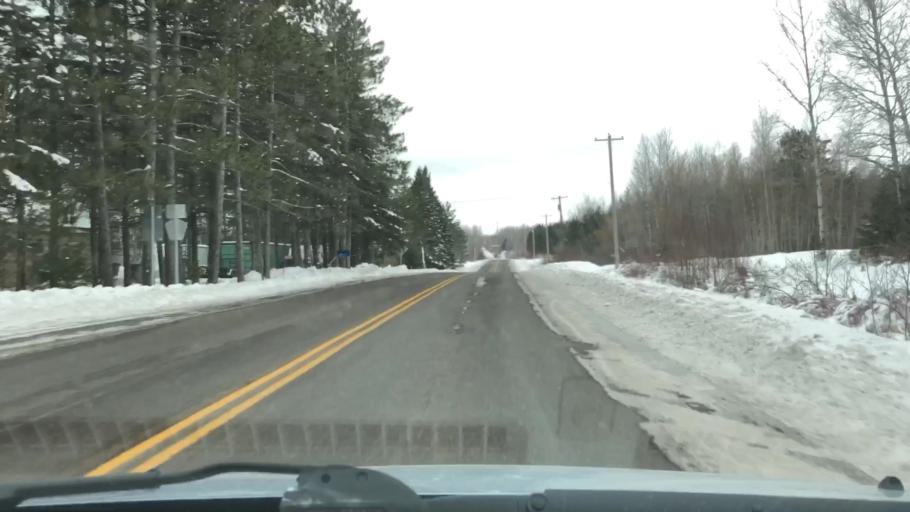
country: US
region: Minnesota
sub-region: Saint Louis County
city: Proctor
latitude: 46.6991
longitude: -92.2802
